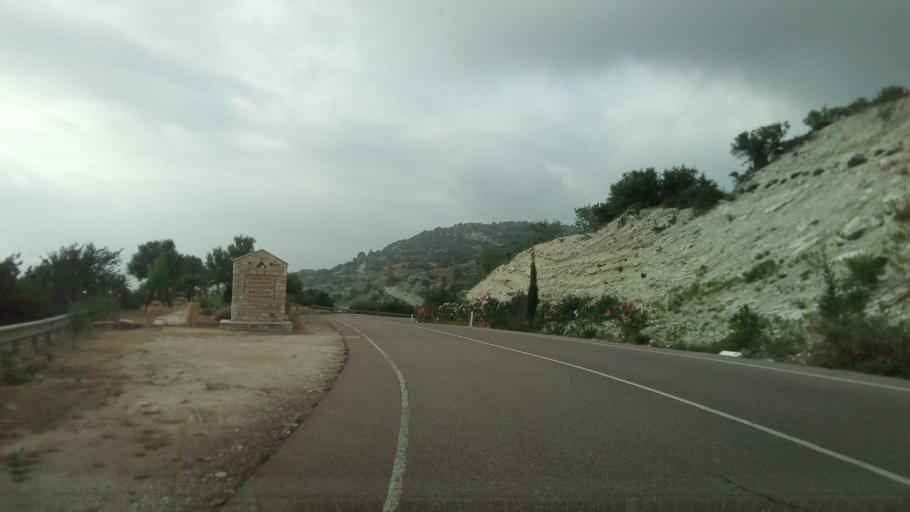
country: CY
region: Limassol
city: Pachna
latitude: 34.8310
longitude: 32.6850
